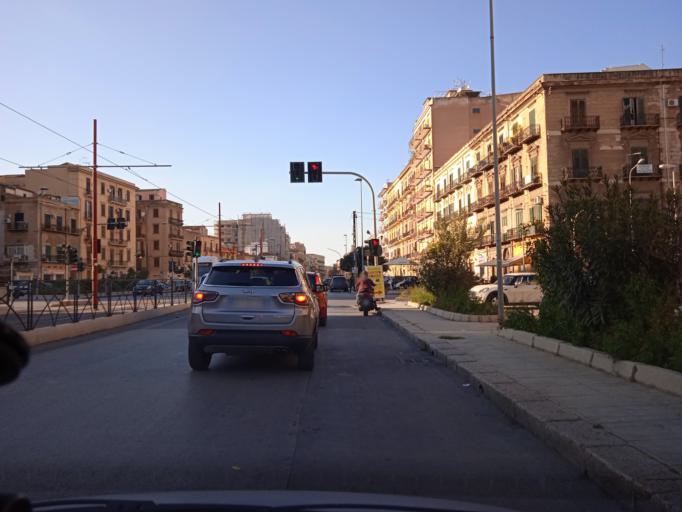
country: IT
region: Sicily
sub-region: Palermo
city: Palermo
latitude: 38.1086
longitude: 13.3710
